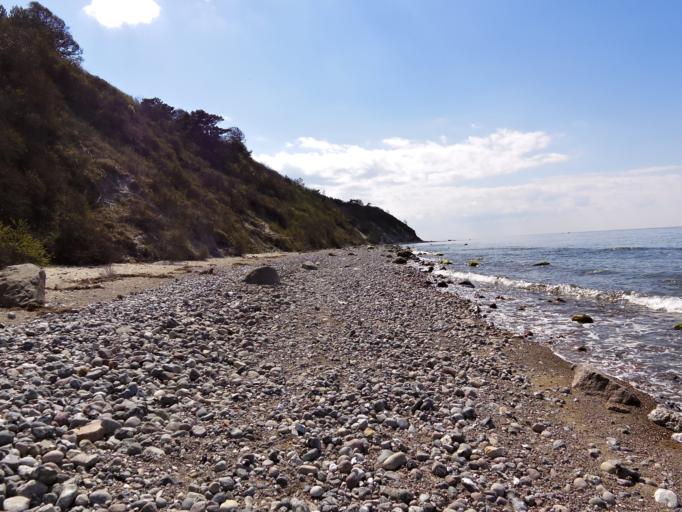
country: DE
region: Mecklenburg-Vorpommern
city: Hiddensee
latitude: 54.5986
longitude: 13.1124
